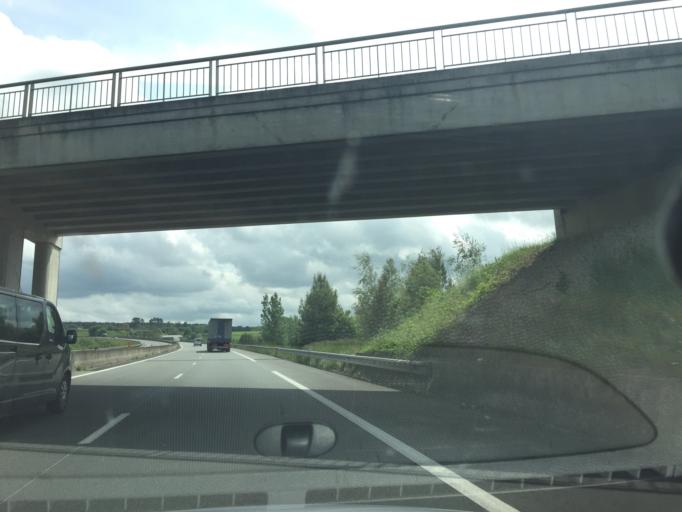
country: FR
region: Pays de la Loire
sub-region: Departement de la Sarthe
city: Ecommoy
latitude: 47.7970
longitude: 0.3022
